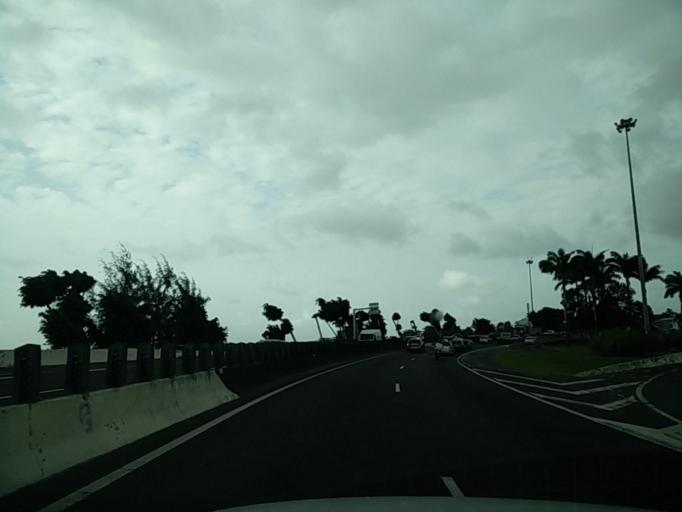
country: GP
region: Guadeloupe
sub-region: Guadeloupe
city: Baie-Mahault
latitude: 16.2505
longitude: -61.5893
